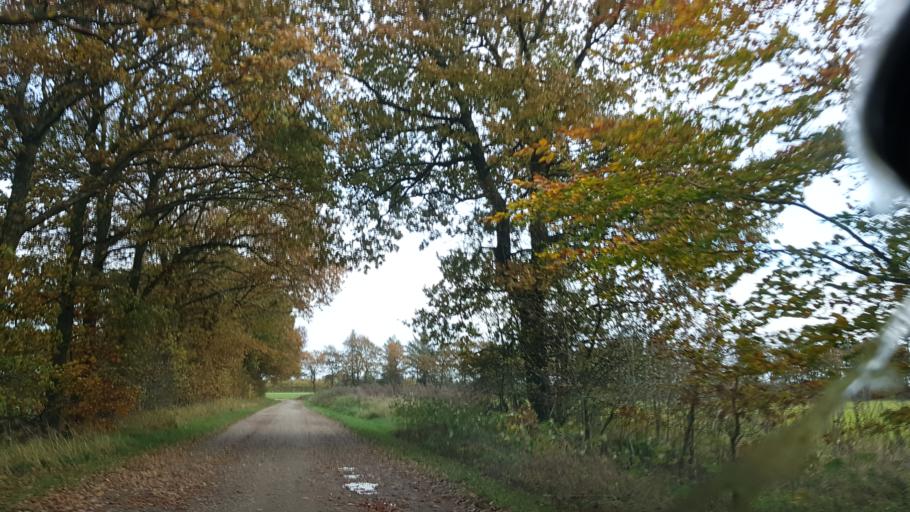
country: DK
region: South Denmark
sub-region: Haderslev Kommune
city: Vojens
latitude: 55.2912
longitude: 9.2258
